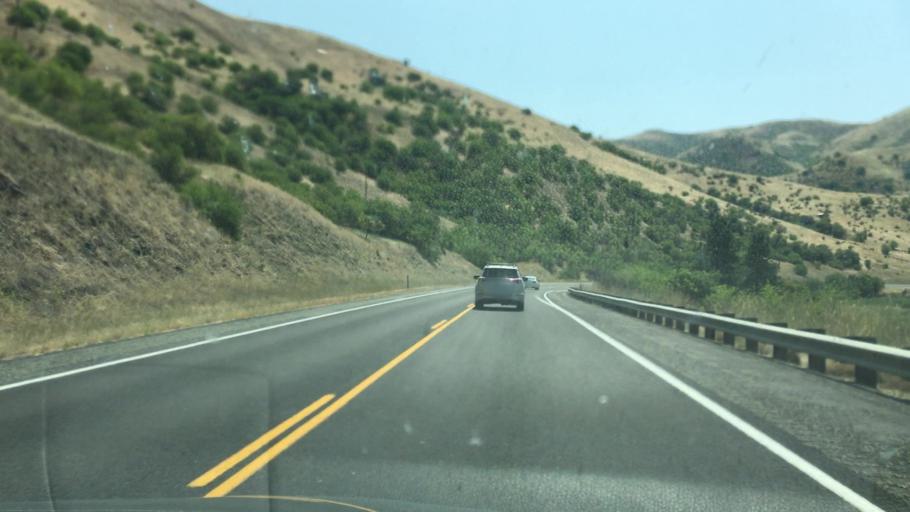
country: US
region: Idaho
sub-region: Idaho County
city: Grangeville
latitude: 45.7298
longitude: -116.3017
